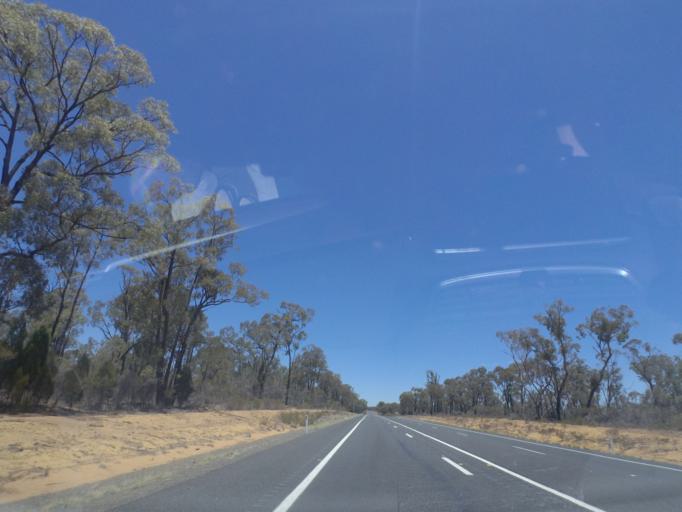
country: AU
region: New South Wales
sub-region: Warrumbungle Shire
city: Coonabarabran
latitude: -30.8767
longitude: 149.4480
